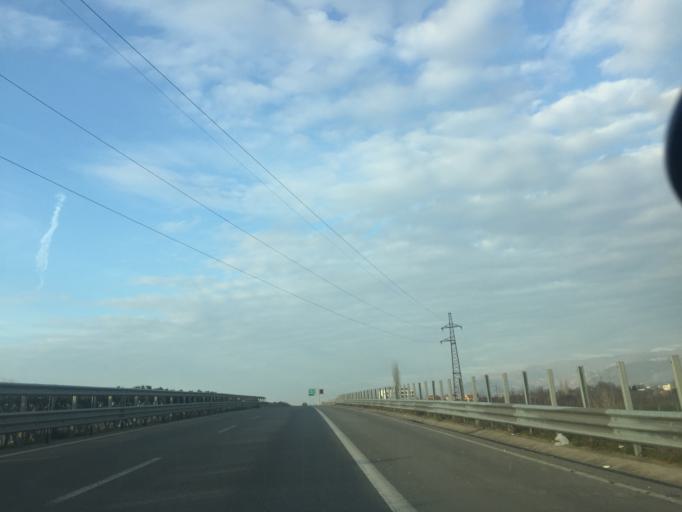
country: AL
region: Durres
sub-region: Rrethi i Krujes
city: Thumane
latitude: 41.5522
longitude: 19.6723
